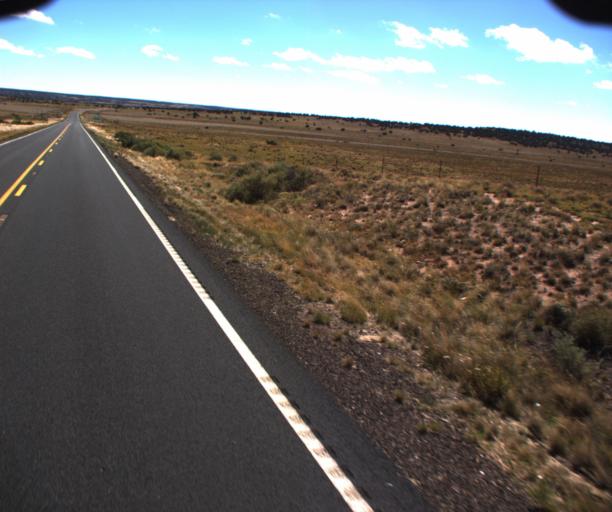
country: US
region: Arizona
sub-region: Apache County
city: Houck
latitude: 35.0325
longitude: -109.2576
